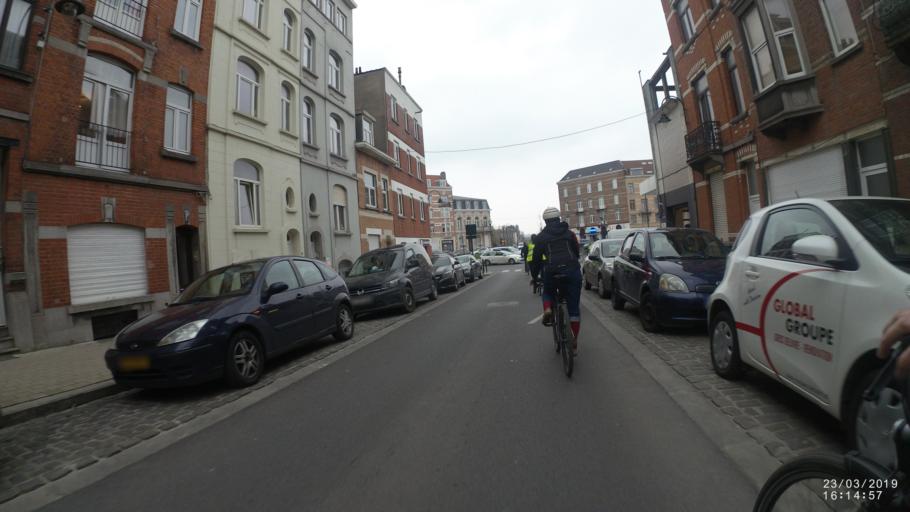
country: BE
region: Brussels Capital
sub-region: Bruxelles-Capitale
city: Brussels
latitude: 50.8733
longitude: 4.3406
